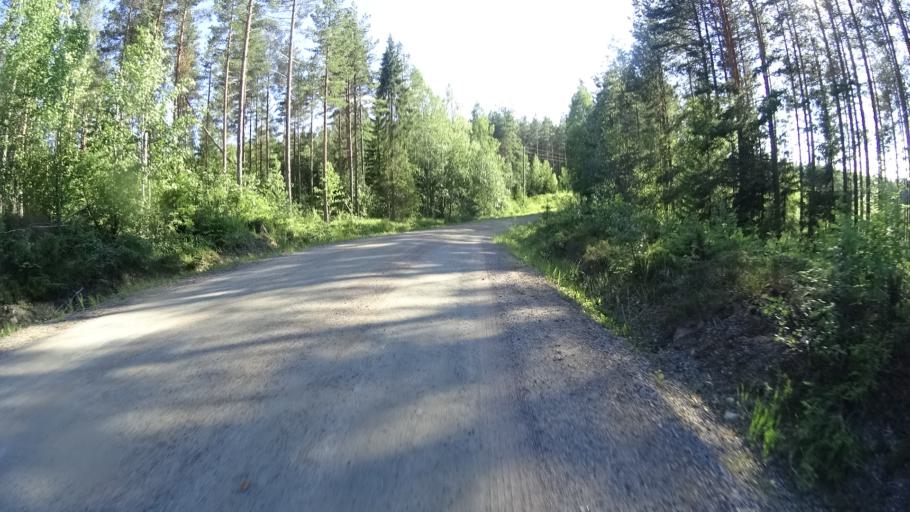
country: FI
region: Uusimaa
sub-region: Helsinki
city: Karkkila
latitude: 60.6482
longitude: 24.1600
